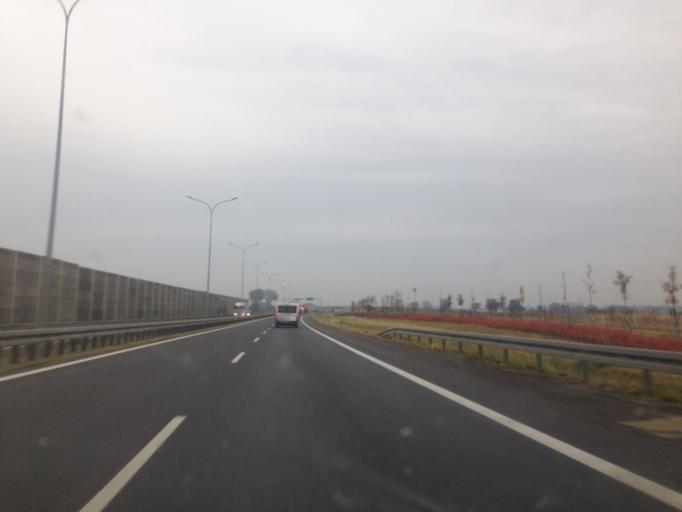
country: PL
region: Greater Poland Voivodeship
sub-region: Powiat poznanski
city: Kostrzyn
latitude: 52.3864
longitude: 17.2485
